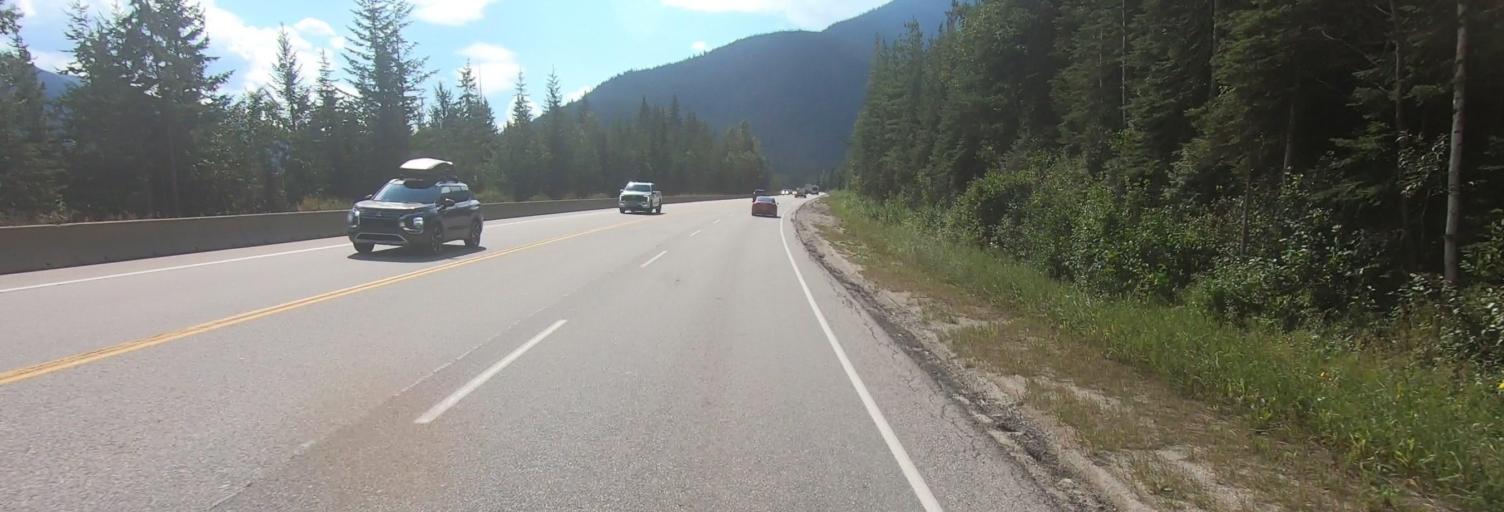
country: CA
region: British Columbia
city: Golden
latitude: 51.3526
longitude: -117.4365
